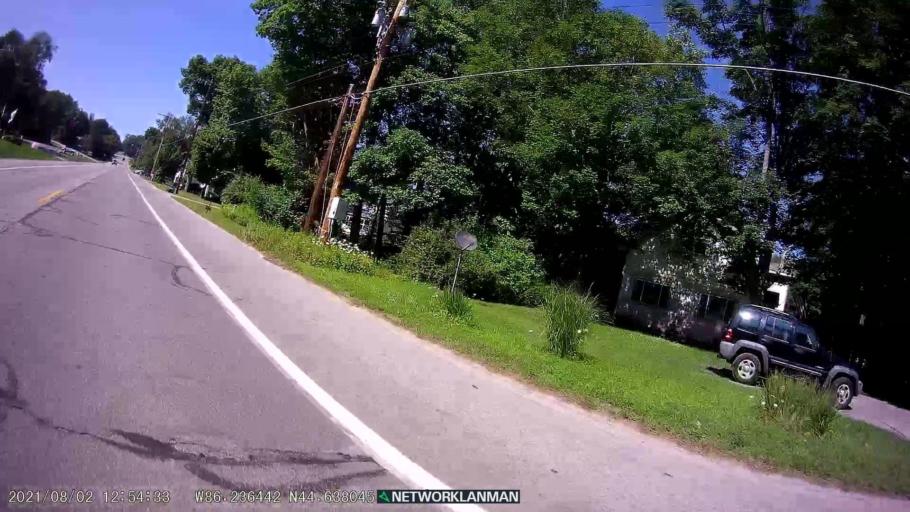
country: US
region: Michigan
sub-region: Benzie County
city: Frankfort
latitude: 44.6382
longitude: -86.2367
